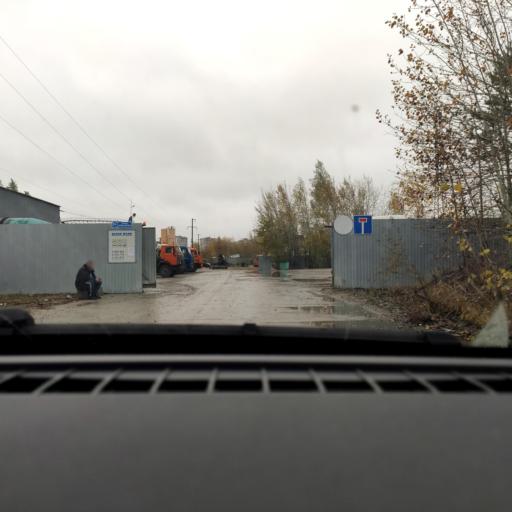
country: RU
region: Voronezj
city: Maslovka
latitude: 51.5928
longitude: 39.2537
